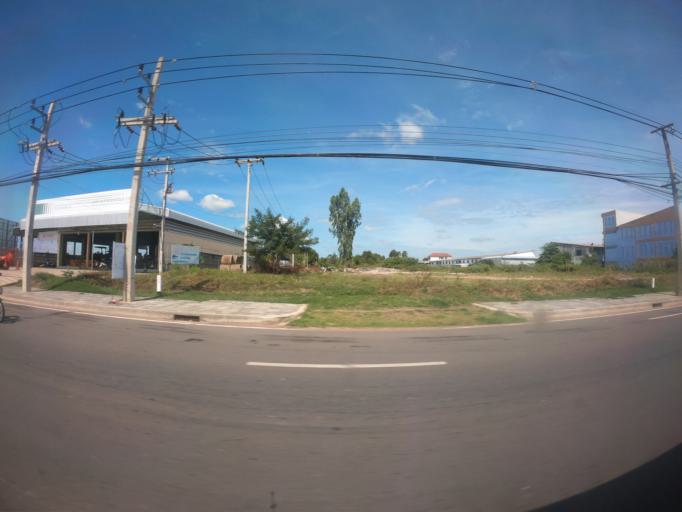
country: TH
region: Surin
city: Prasat
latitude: 14.6274
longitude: 103.4097
